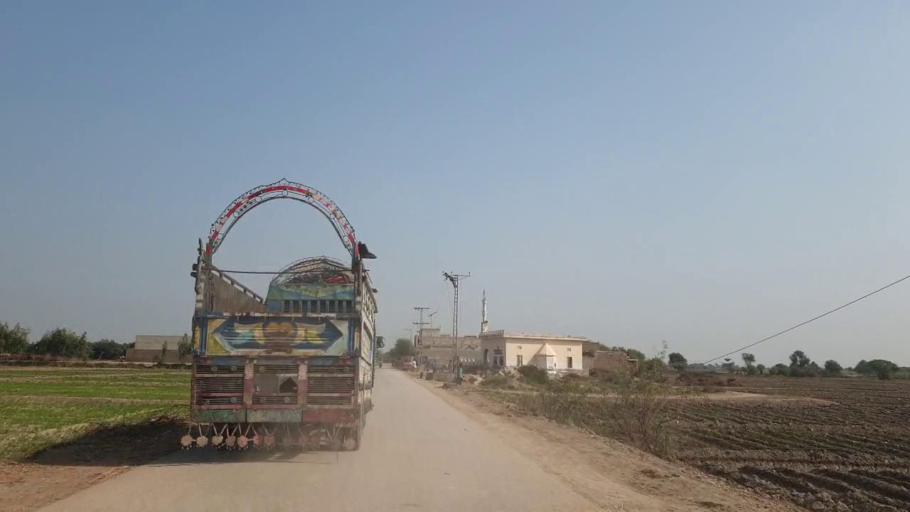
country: PK
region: Sindh
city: Matiari
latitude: 25.5016
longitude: 68.4576
